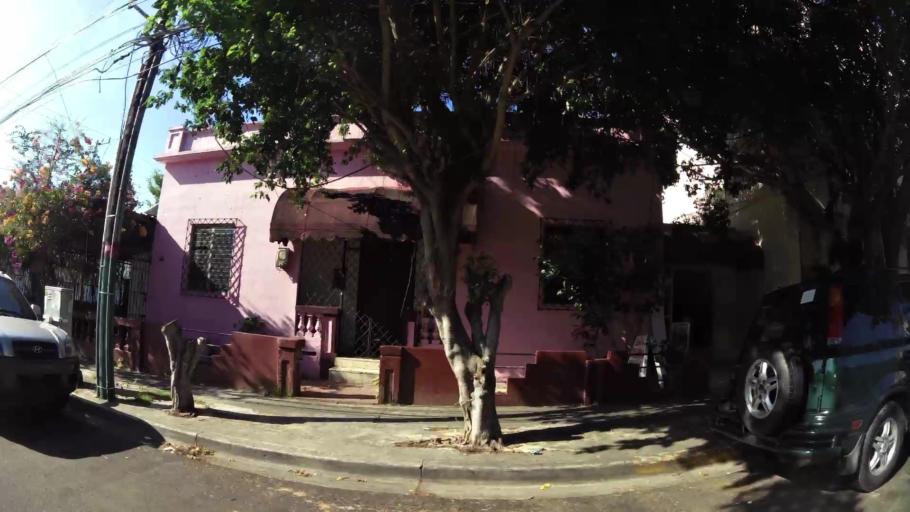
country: DO
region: Nacional
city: Ciudad Nueva
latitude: 18.4700
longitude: -69.8949
